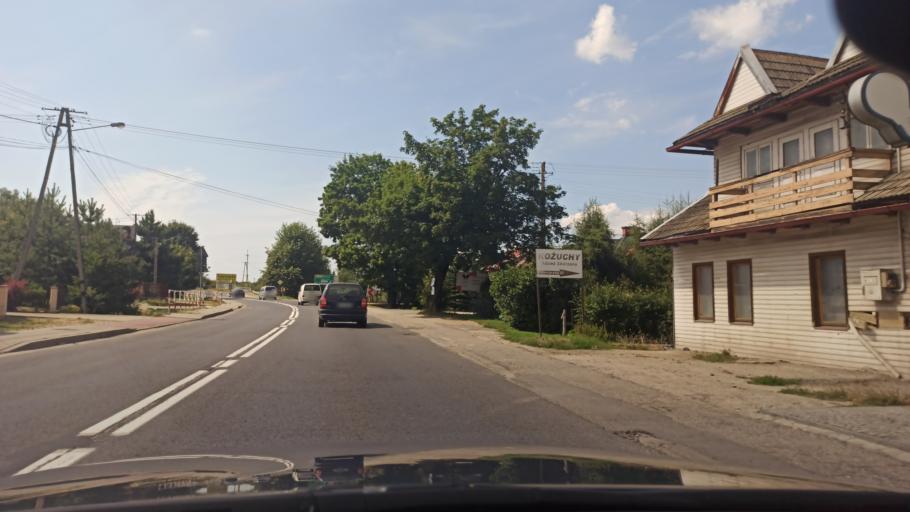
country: PL
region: Lesser Poland Voivodeship
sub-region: Powiat nowotarski
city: Waksmund
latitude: 49.4832
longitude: 20.0683
